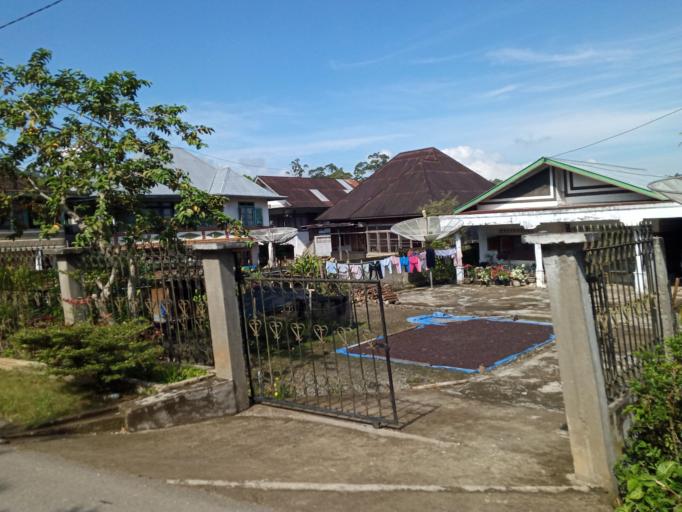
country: ID
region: Jambi
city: Sungai Penuh
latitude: -2.1693
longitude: 101.5972
